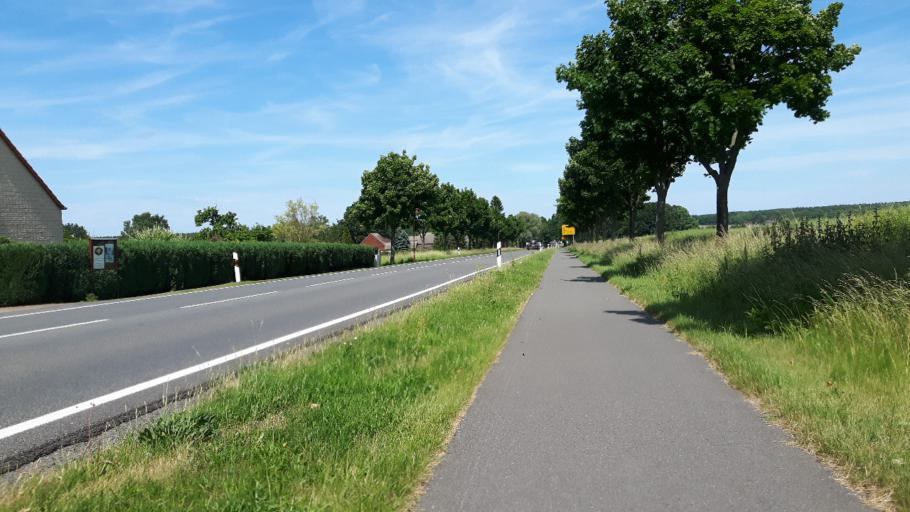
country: DE
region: Saxony-Anhalt
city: Kropstadt
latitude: 52.0244
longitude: 12.7972
